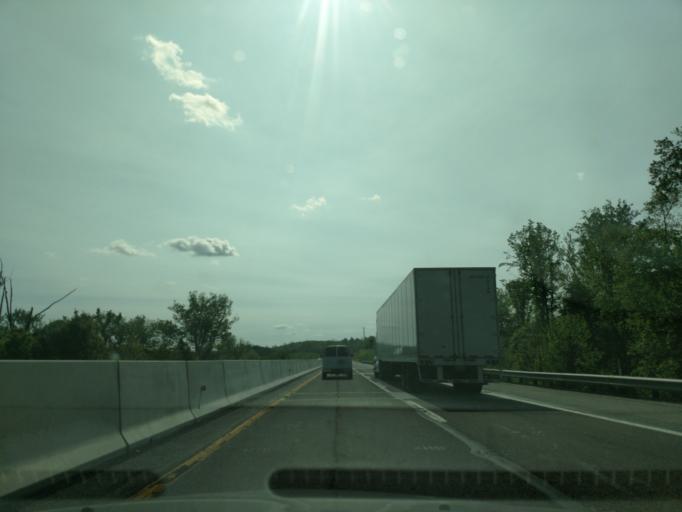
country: US
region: Pennsylvania
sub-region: Lancaster County
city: Brickerville
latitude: 40.2364
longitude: -76.2801
